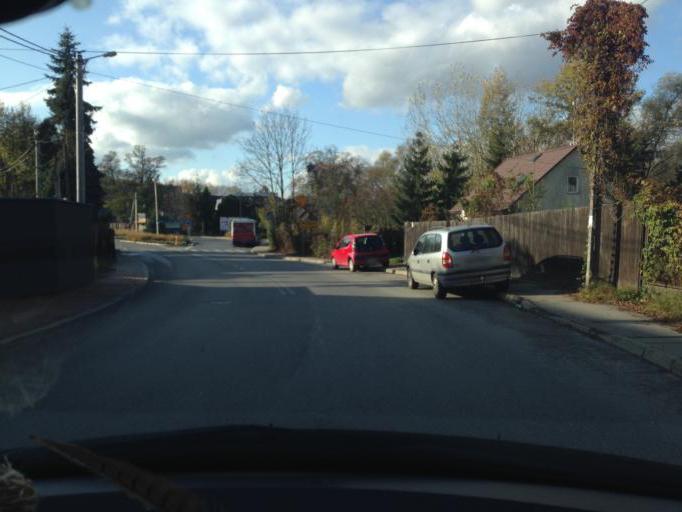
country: PL
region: Lesser Poland Voivodeship
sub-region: Powiat krakowski
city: Rzaska
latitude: 50.0679
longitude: 19.8485
